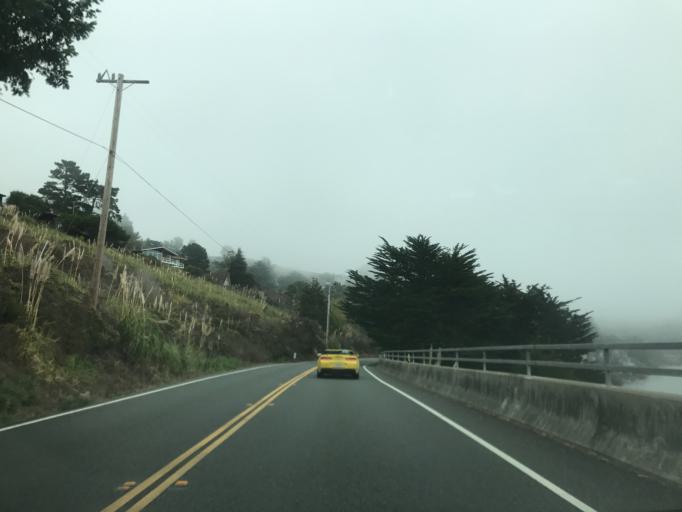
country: US
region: California
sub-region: Sonoma County
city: Monte Rio
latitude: 38.4504
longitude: -123.1226
